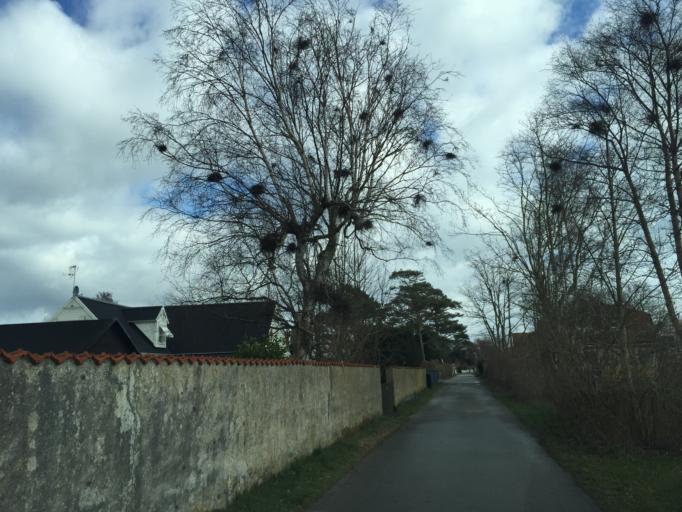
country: SE
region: Skane
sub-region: Vellinge Kommun
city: Skanor med Falsterbo
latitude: 55.3982
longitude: 12.8325
